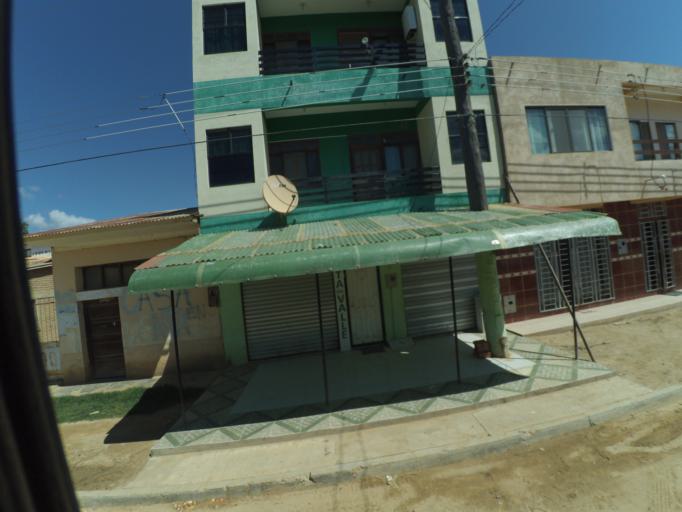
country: BO
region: Santa Cruz
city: Comarapa
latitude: -18.0966
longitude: -64.5883
